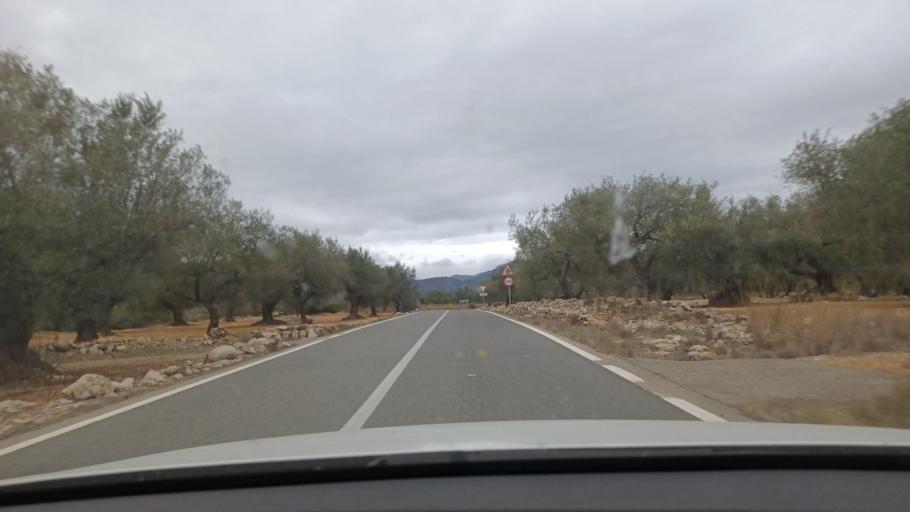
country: ES
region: Catalonia
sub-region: Provincia de Tarragona
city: Mas de Barberans
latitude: 40.6396
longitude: 0.3543
